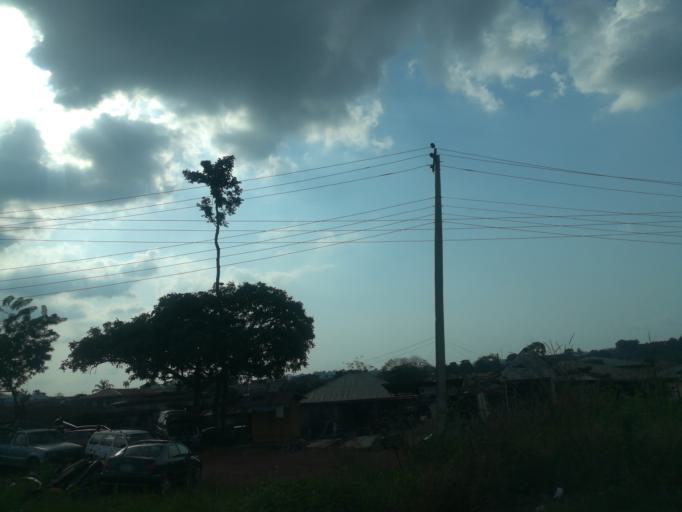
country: NG
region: Oyo
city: Moniya
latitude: 7.4822
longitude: 3.9140
